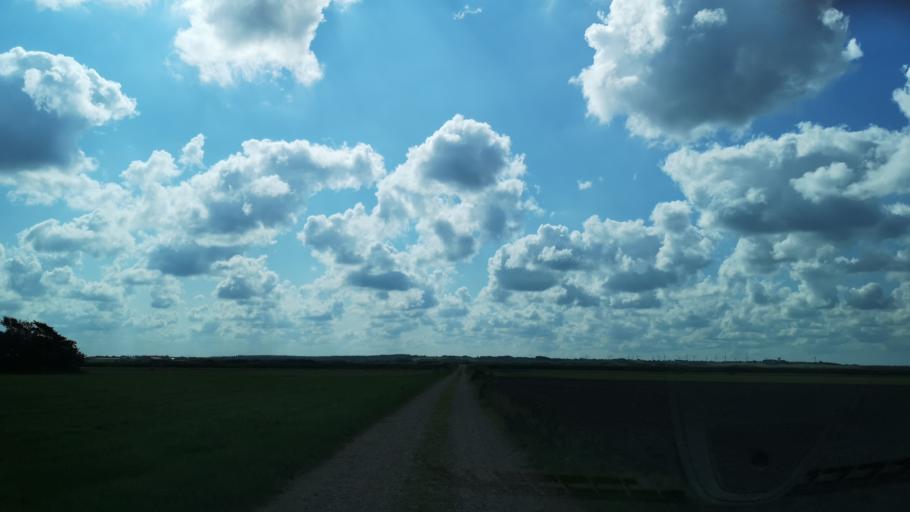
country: DK
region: Central Jutland
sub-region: Ringkobing-Skjern Kommune
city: Skjern
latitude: 55.9314
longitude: 8.4610
